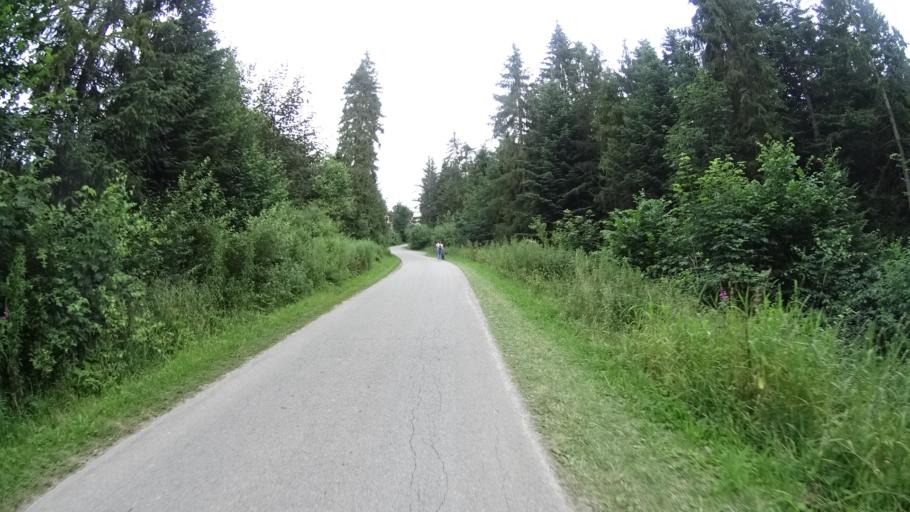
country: PL
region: Lesser Poland Voivodeship
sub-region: Powiat nowotarski
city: Krosnica
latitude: 49.4394
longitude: 20.3278
